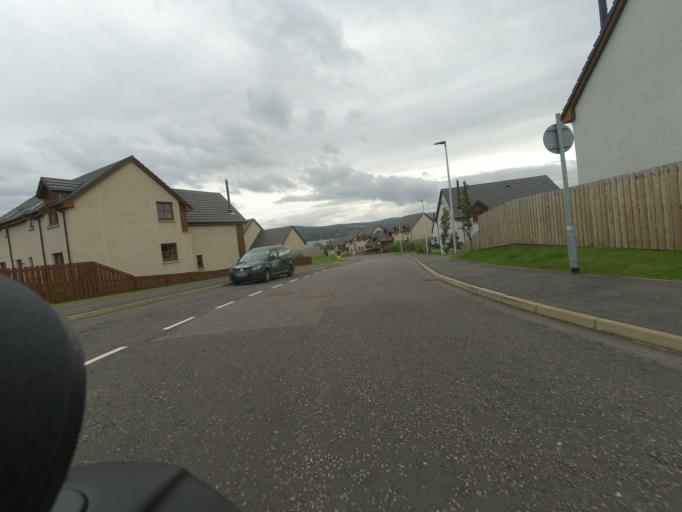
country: GB
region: Scotland
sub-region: Highland
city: Inverness
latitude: 57.5067
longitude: -4.2726
